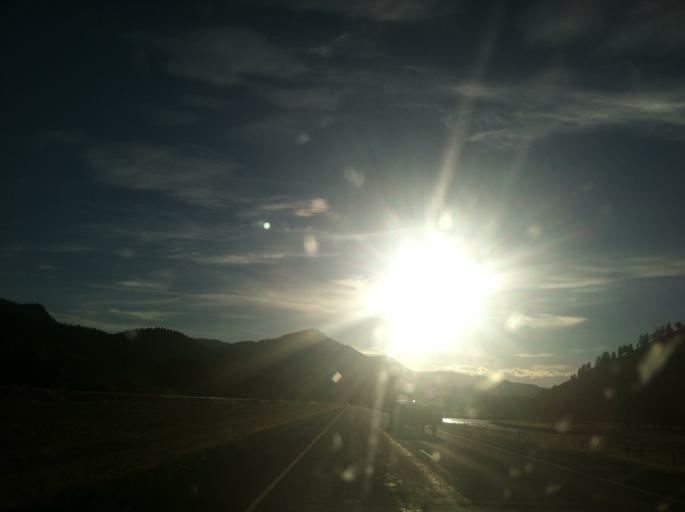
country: US
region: Montana
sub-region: Missoula County
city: Clinton
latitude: 46.6974
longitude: -113.4024
